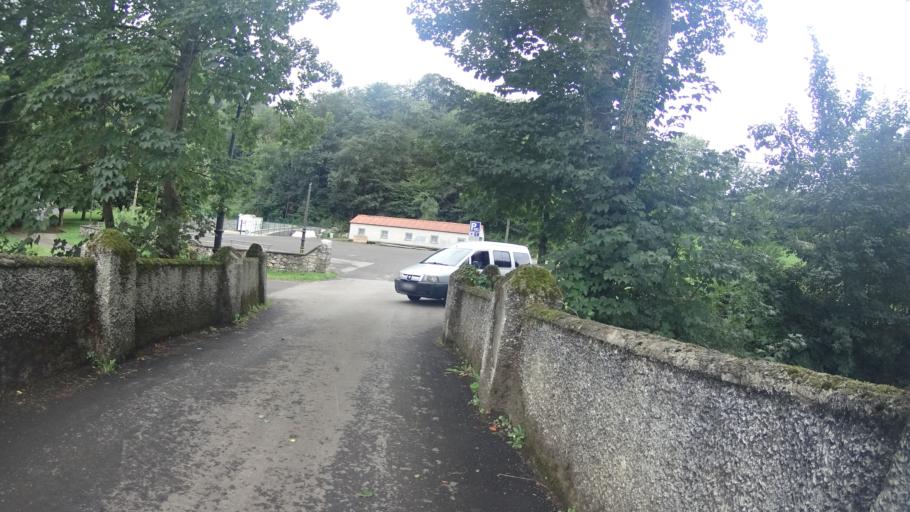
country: ES
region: Asturias
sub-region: Province of Asturias
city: Carrena
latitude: 43.3351
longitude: -4.9731
